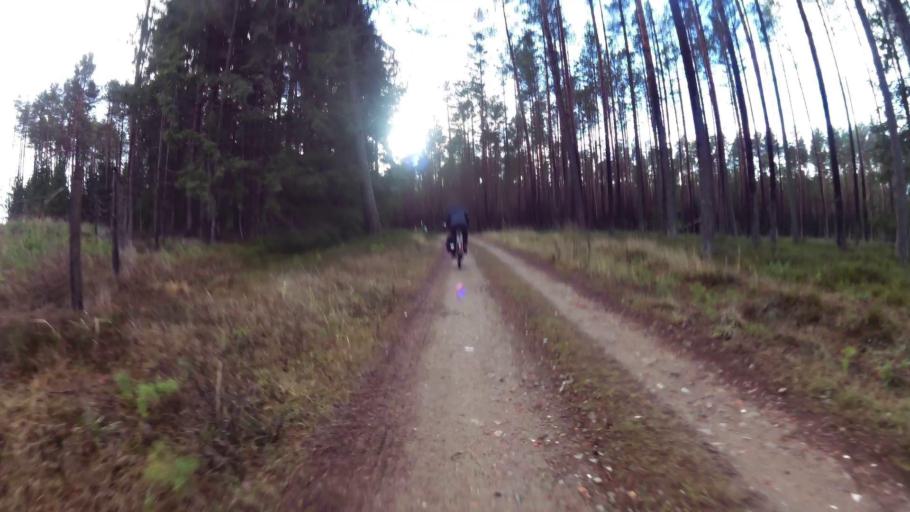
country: PL
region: West Pomeranian Voivodeship
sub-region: Powiat koszalinski
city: Sianow
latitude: 54.0845
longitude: 16.2911
